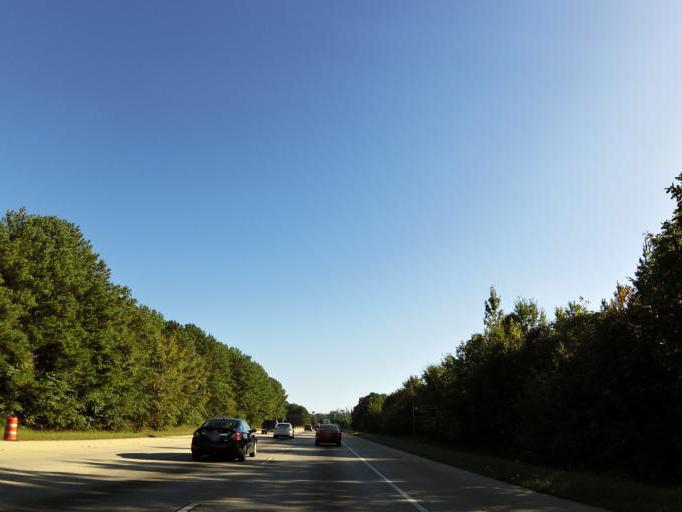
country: US
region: Georgia
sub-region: Cobb County
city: Kennesaw
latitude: 34.0180
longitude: -84.5706
